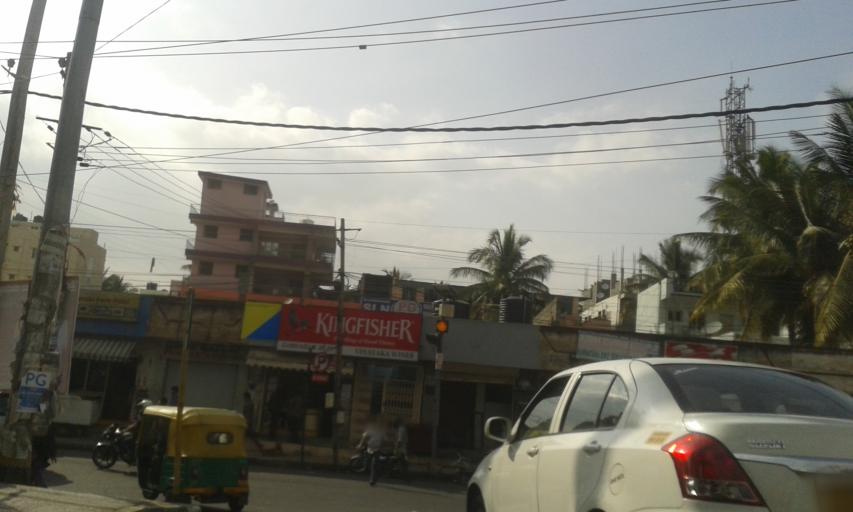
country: IN
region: Karnataka
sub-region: Bangalore Urban
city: Bangalore
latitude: 12.9311
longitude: 77.6101
